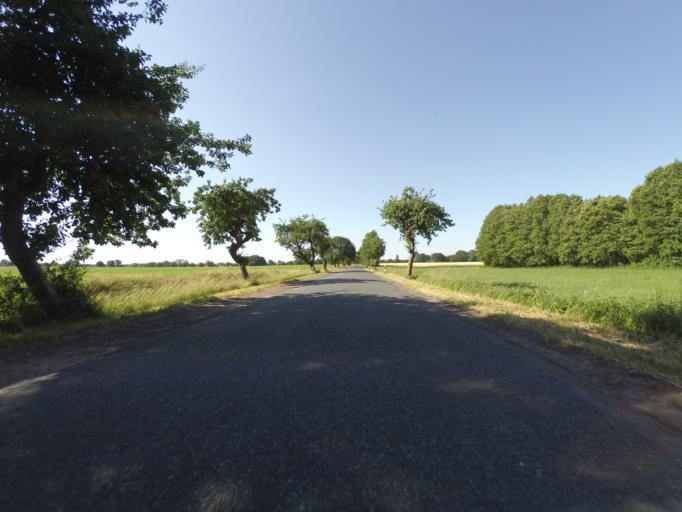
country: DE
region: Brandenburg
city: Triglitz
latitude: 53.2229
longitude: 12.1127
